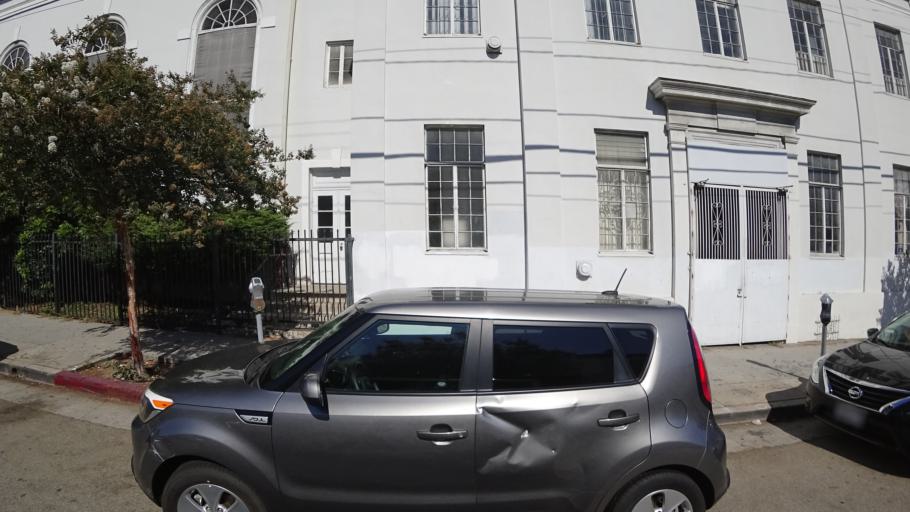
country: US
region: California
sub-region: Los Angeles County
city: Hollywood
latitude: 34.0993
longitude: -118.3363
